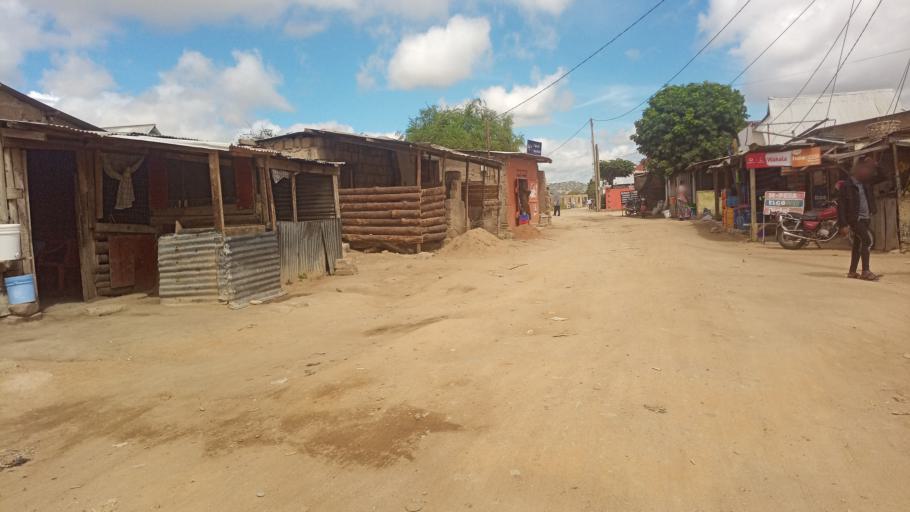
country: TZ
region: Dodoma
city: Kisasa
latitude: -6.1756
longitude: 35.7665
